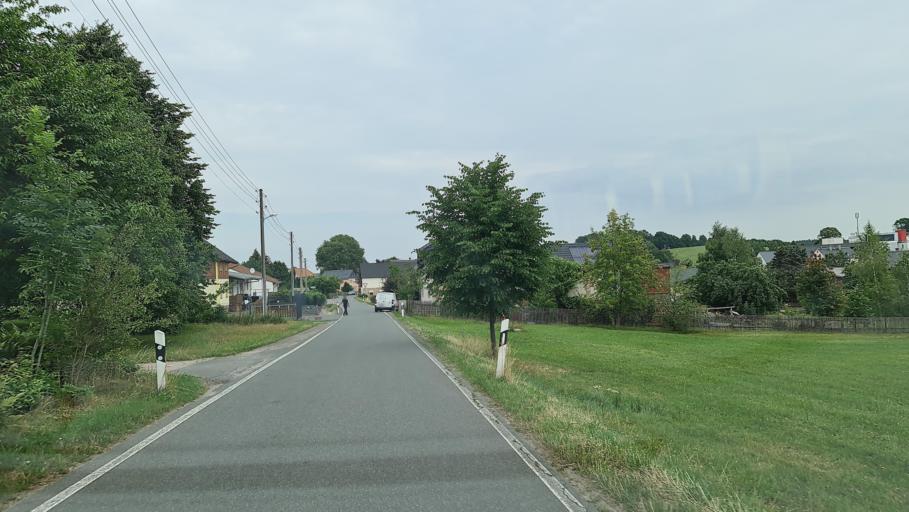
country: DE
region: Saxony
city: Hirschfeld
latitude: 50.5810
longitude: 12.4471
